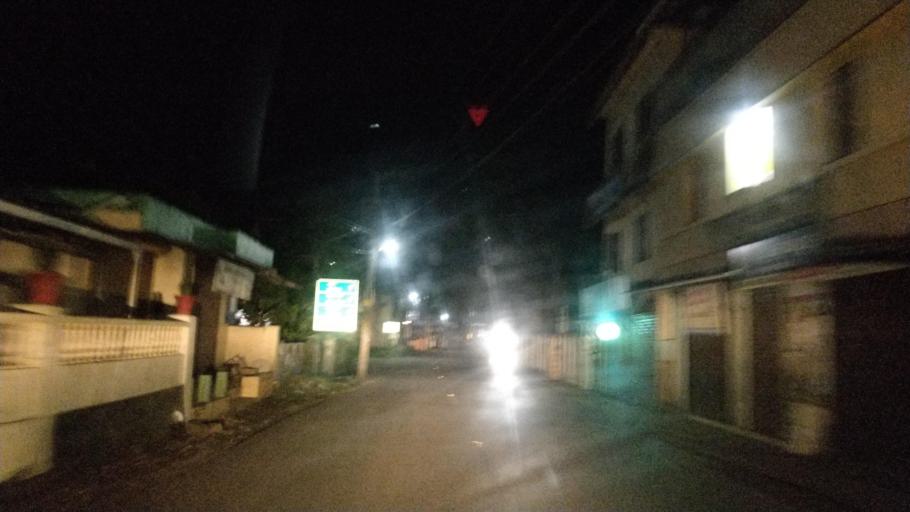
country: IN
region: Kerala
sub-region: Kottayam
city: Kottayam
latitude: 9.6786
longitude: 76.5058
